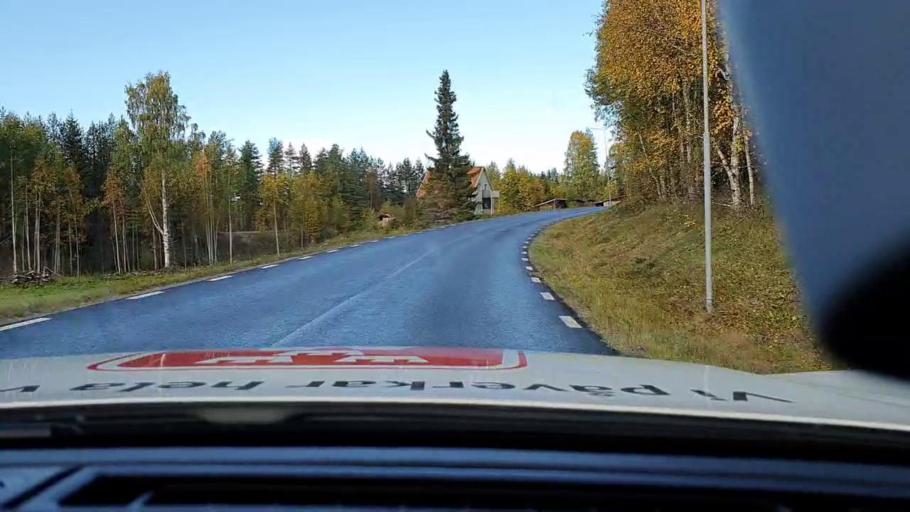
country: SE
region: Vaesterbotten
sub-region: Skelleftea Kommun
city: Langsele
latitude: 64.9474
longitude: 20.0222
